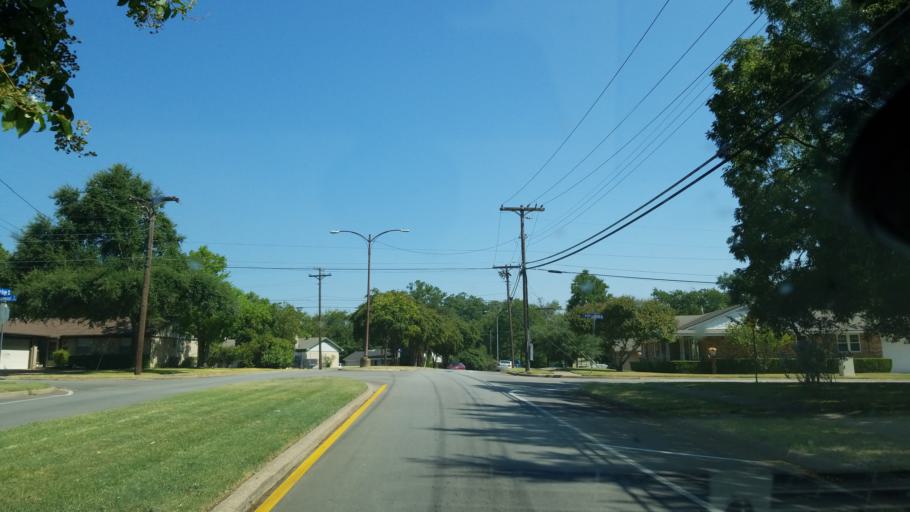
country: US
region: Texas
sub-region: Dallas County
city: Duncanville
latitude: 32.6543
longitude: -96.9023
